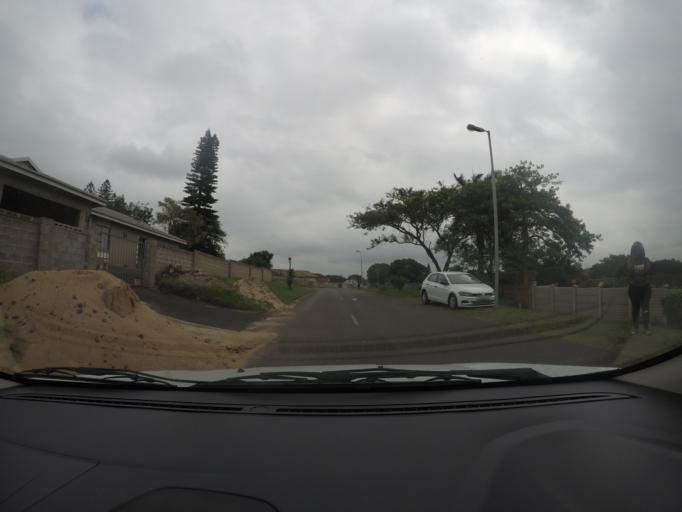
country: ZA
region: KwaZulu-Natal
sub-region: uThungulu District Municipality
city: Empangeni
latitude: -28.7370
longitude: 31.8987
